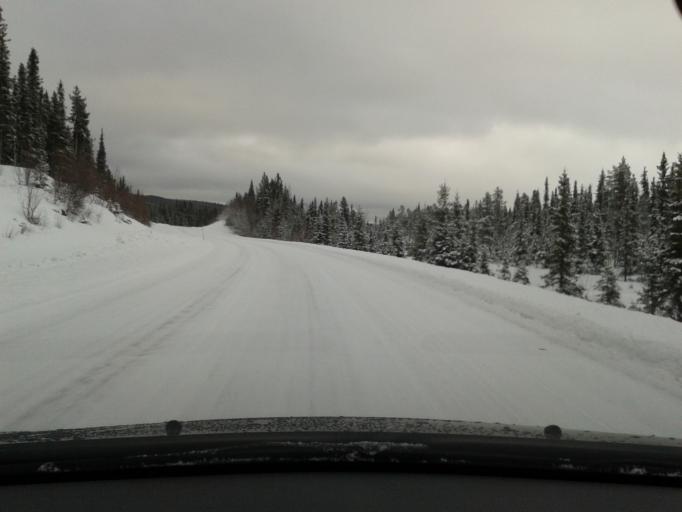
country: SE
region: Vaesterbotten
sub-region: Vilhelmina Kommun
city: Sjoberg
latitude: 65.2375
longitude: 15.7921
